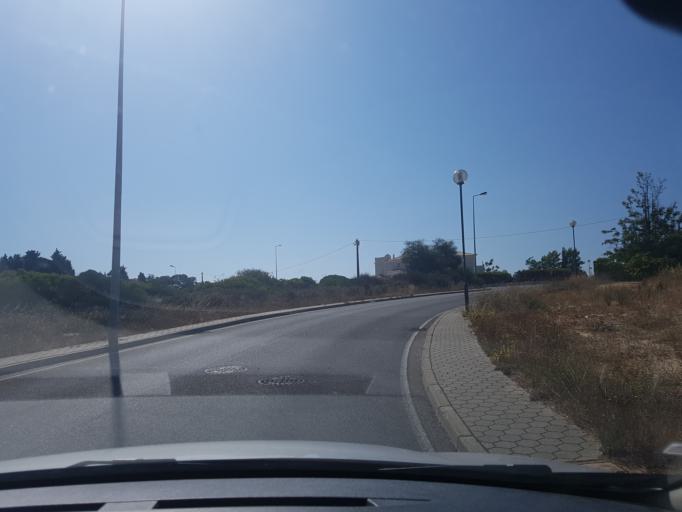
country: PT
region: Faro
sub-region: Lagoa
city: Carvoeiro
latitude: 37.1015
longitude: -8.4521
